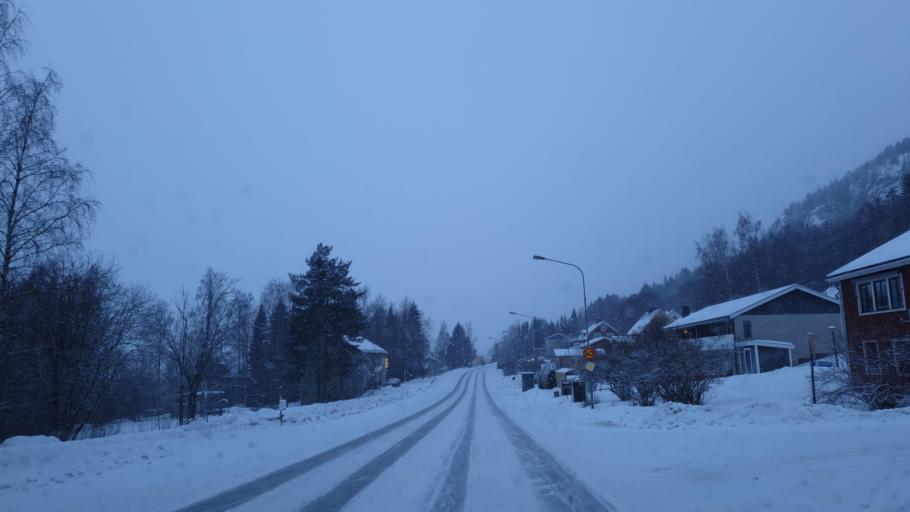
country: SE
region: Vaesternorrland
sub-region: OErnskoeldsviks Kommun
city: Ornskoldsvik
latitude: 63.2982
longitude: 18.6702
